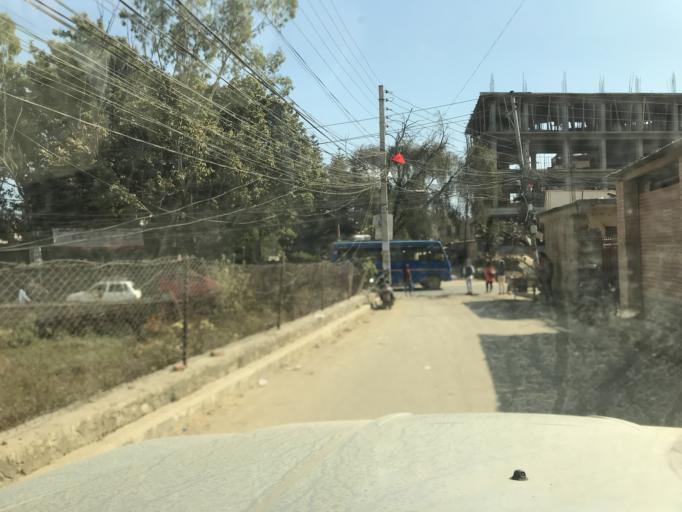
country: NP
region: Central Region
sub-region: Bagmati Zone
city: Patan
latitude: 27.6435
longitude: 85.3187
